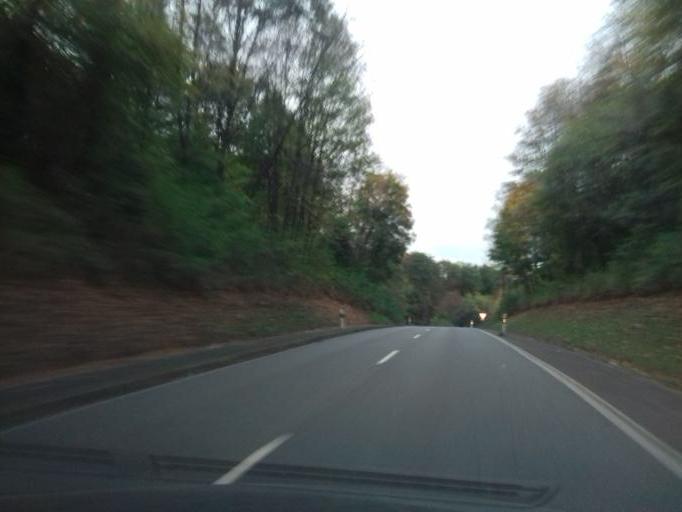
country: DE
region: Rheinland-Pfalz
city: Tawern
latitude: 49.6593
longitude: 6.5273
